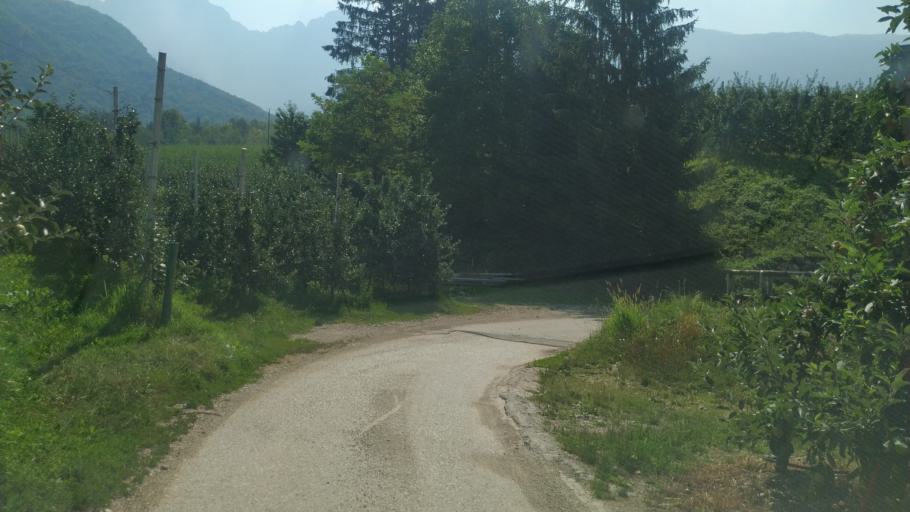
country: IT
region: Trentino-Alto Adige
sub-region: Provincia di Trento
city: Vigo di Ton
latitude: 46.2779
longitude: 11.0832
